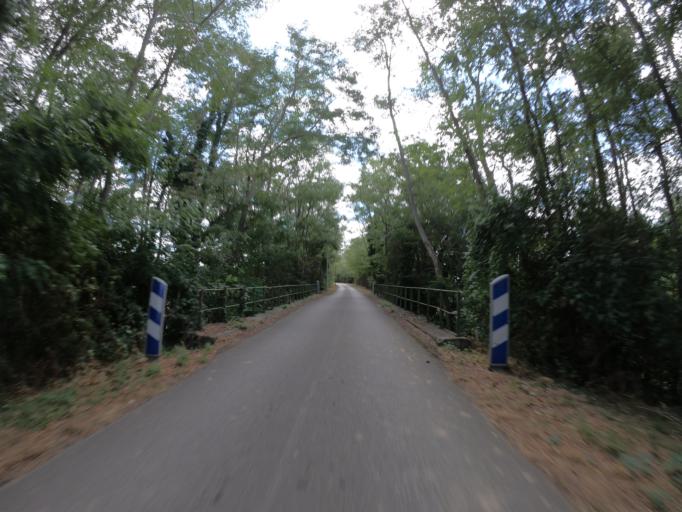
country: FR
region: Midi-Pyrenees
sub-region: Departement de l'Ariege
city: La Tour-du-Crieu
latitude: 43.1004
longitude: 1.7293
